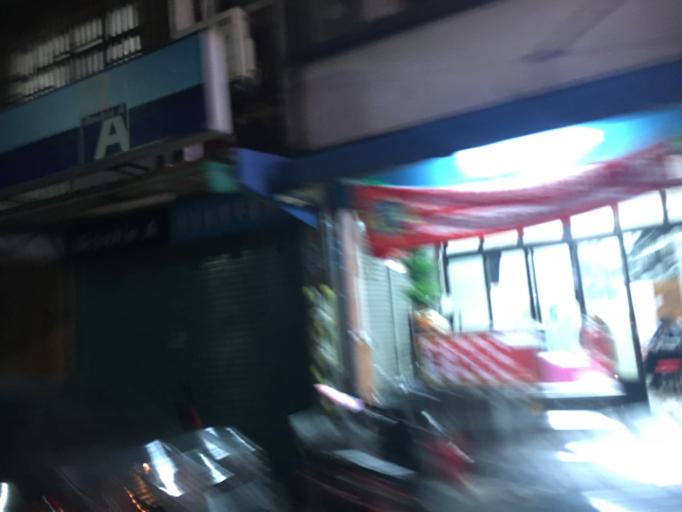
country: TW
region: Taiwan
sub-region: Hsinchu
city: Hsinchu
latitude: 24.7961
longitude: 120.9825
